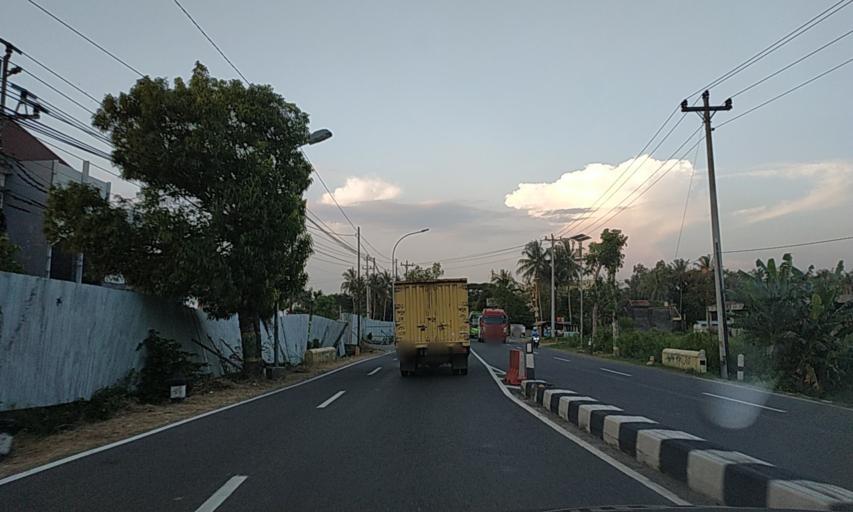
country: ID
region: Daerah Istimewa Yogyakarta
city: Srandakan
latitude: -7.8773
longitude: 110.1332
